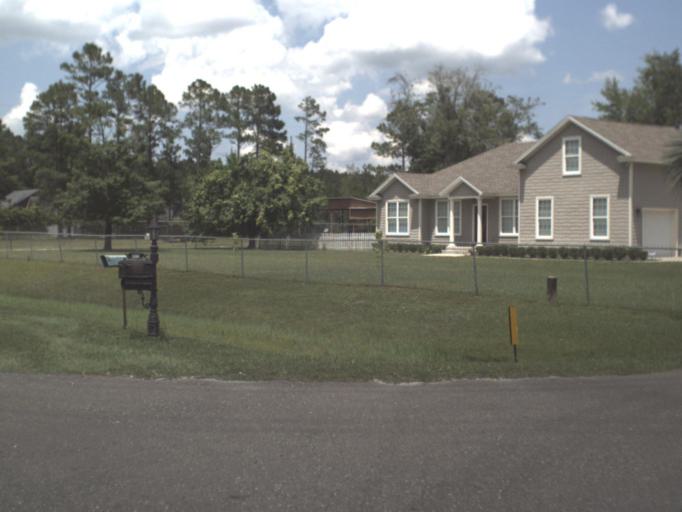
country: US
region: Florida
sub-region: Baker County
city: Macclenny
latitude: 30.3023
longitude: -82.1258
